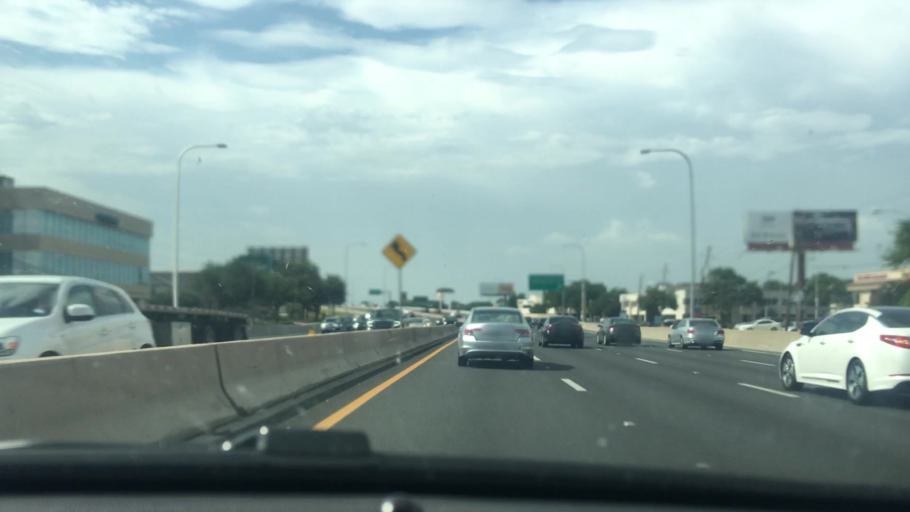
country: US
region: Texas
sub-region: Dallas County
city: Addison
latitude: 32.9861
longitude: -96.8285
